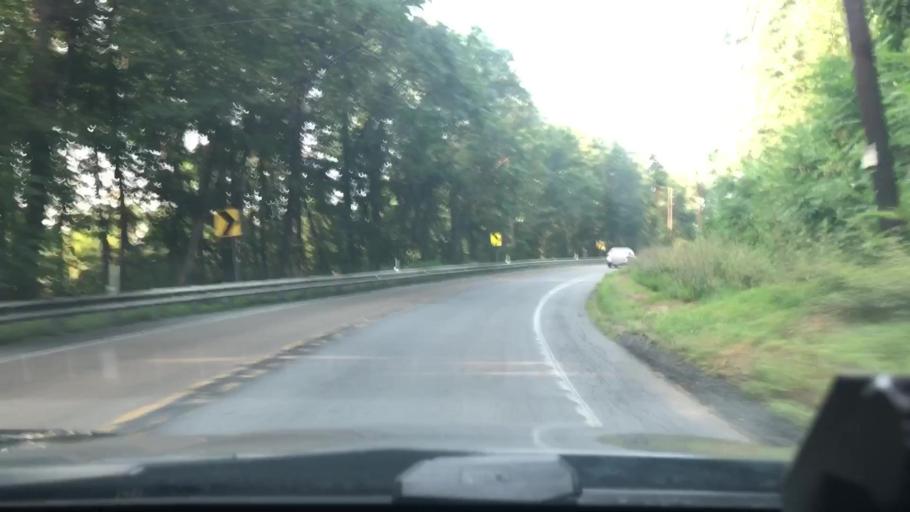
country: US
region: Pennsylvania
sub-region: Berks County
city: Kutztown
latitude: 40.5667
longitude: -75.8104
